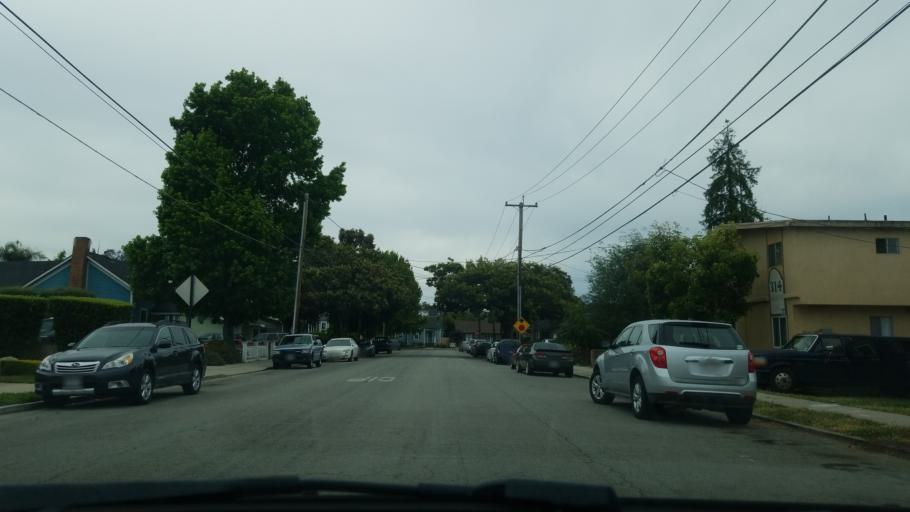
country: US
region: California
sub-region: San Luis Obispo County
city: Arroyo Grande
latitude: 35.1216
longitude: -120.5744
